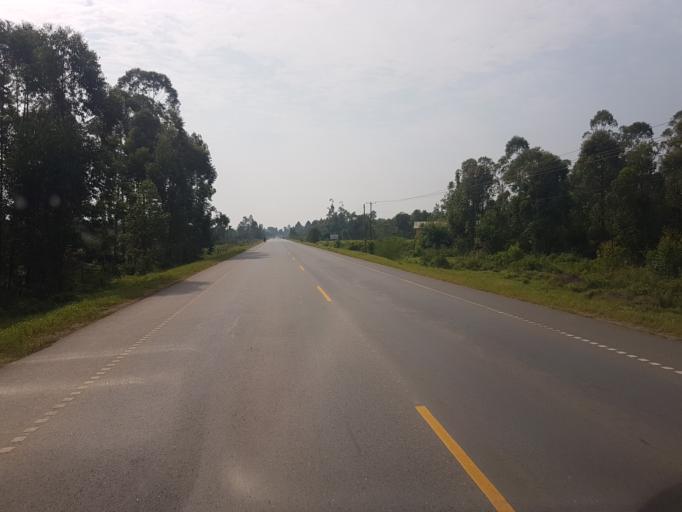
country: UG
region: Western Region
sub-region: Sheema District
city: Kibingo
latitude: -0.6349
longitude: 30.5289
